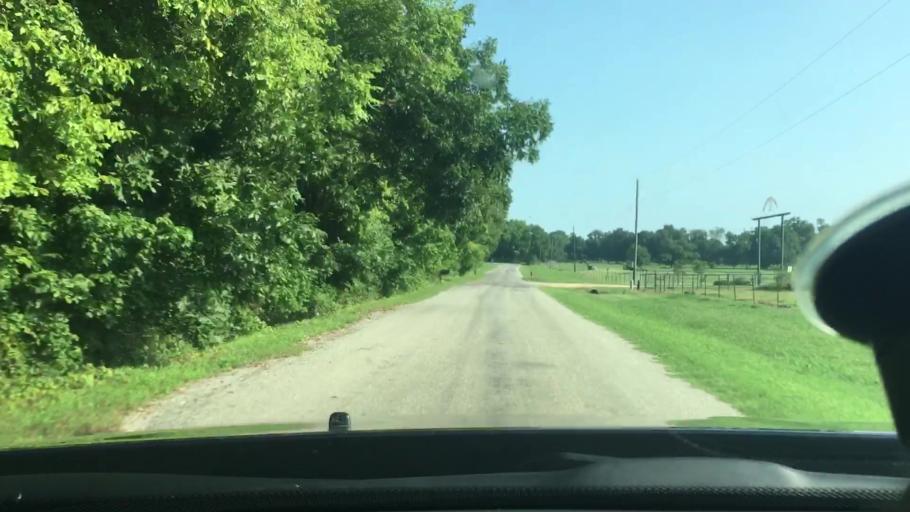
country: US
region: Oklahoma
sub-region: Johnston County
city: Tishomingo
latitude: 34.2126
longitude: -96.6691
